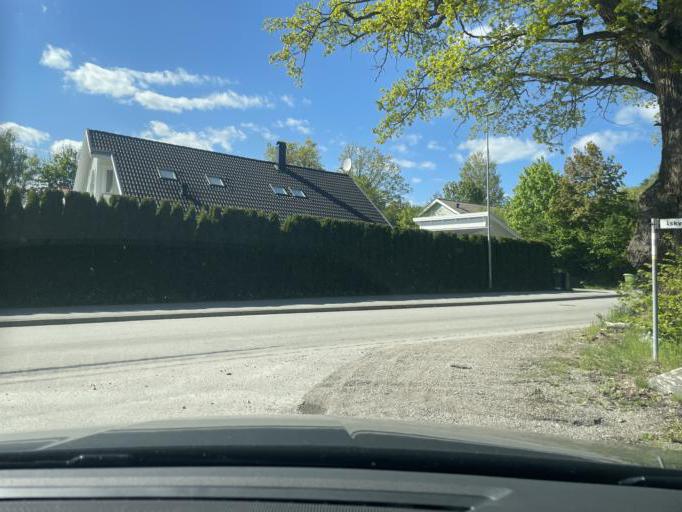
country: SE
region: Stockholm
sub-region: Botkyrka Kommun
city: Tullinge
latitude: 59.2193
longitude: 17.9001
